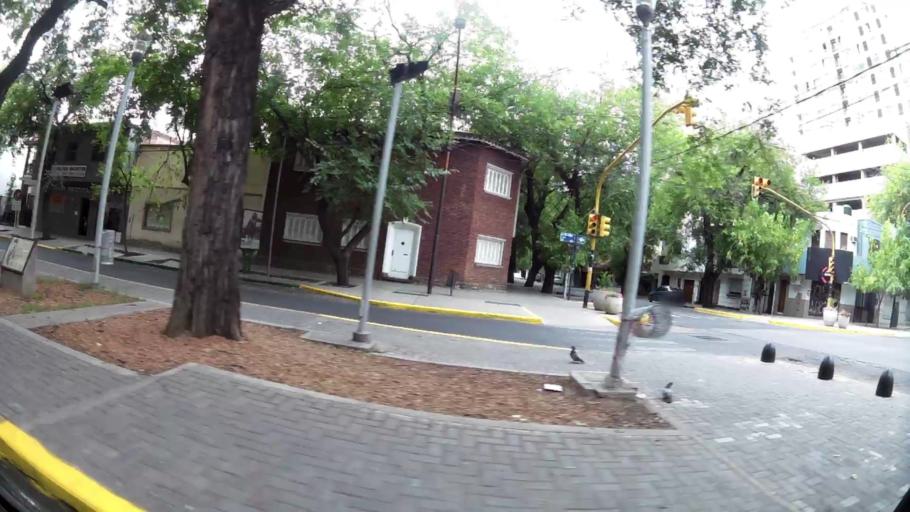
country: AR
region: Mendoza
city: Mendoza
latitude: -32.8929
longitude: -68.8454
